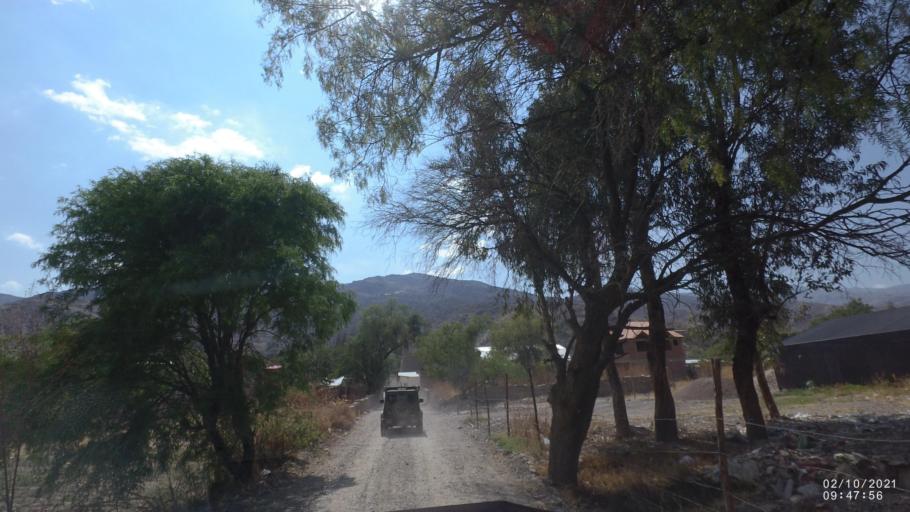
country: BO
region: Cochabamba
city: Irpa Irpa
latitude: -17.8011
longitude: -66.3353
